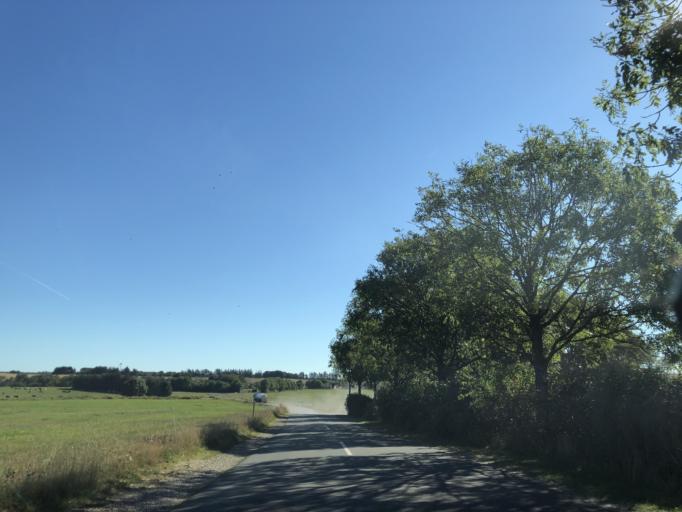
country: DK
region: Central Jutland
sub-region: Holstebro Kommune
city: Ulfborg
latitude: 56.2050
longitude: 8.4782
